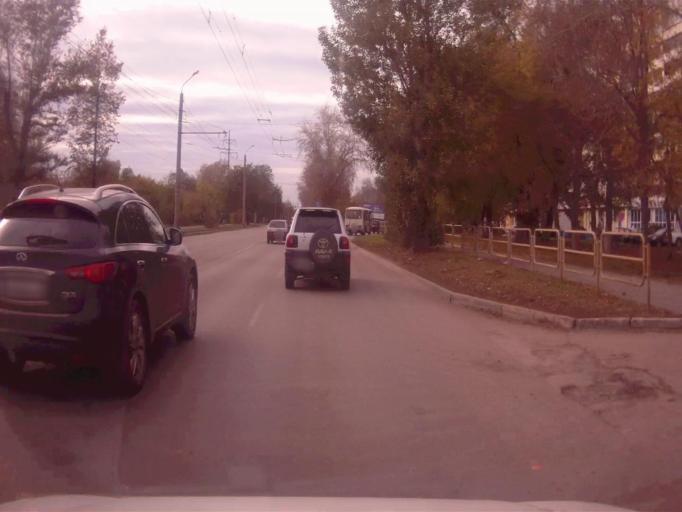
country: RU
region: Chelyabinsk
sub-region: Gorod Chelyabinsk
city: Chelyabinsk
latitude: 55.1166
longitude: 61.4406
